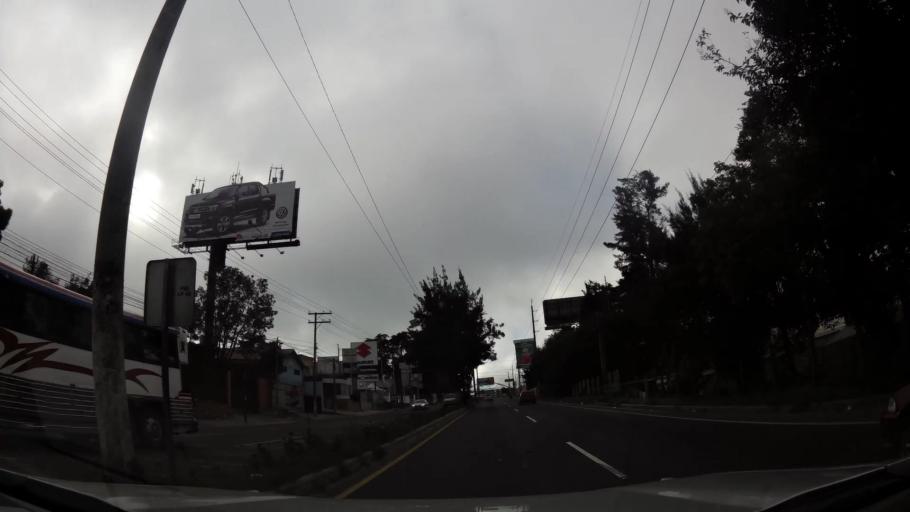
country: GT
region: Guatemala
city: San Jose Pinula
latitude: 14.5464
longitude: -90.4545
